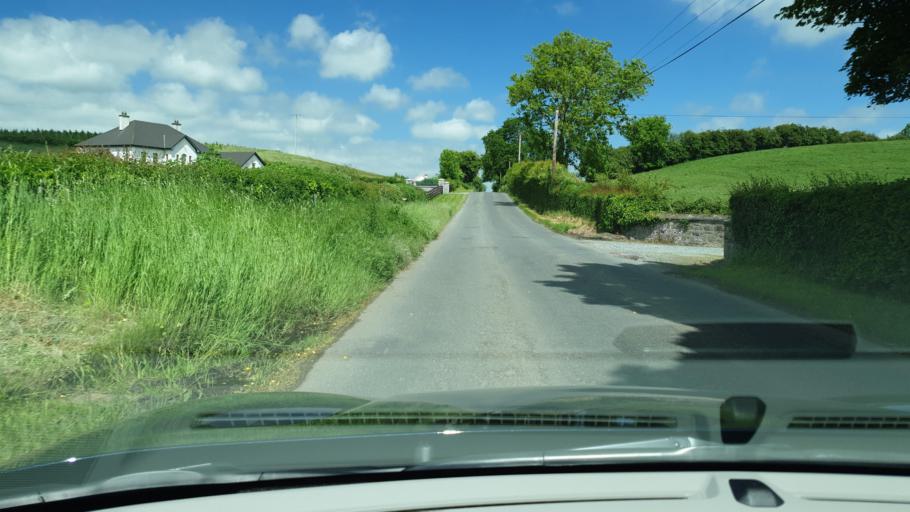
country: IE
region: Leinster
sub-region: Lu
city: Ardee
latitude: 53.8330
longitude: -6.6559
